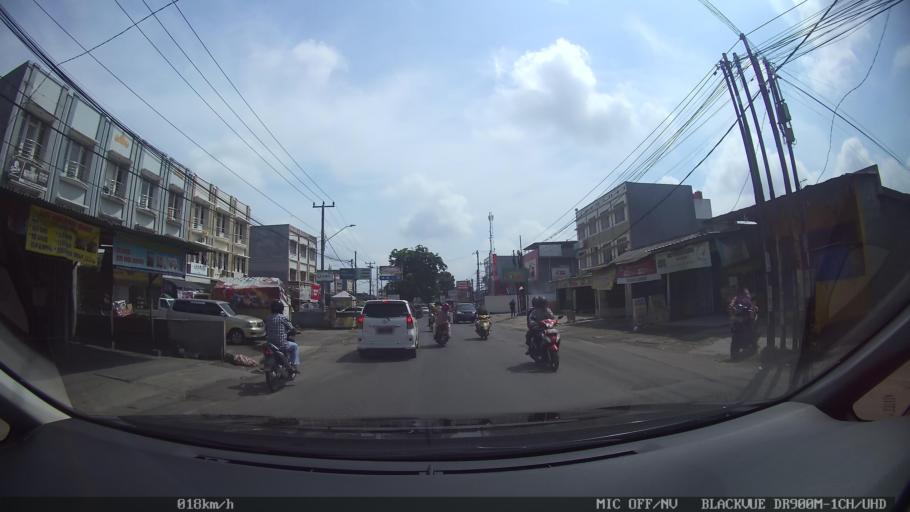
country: ID
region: Lampung
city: Kedaton
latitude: -5.3661
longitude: 105.2752
